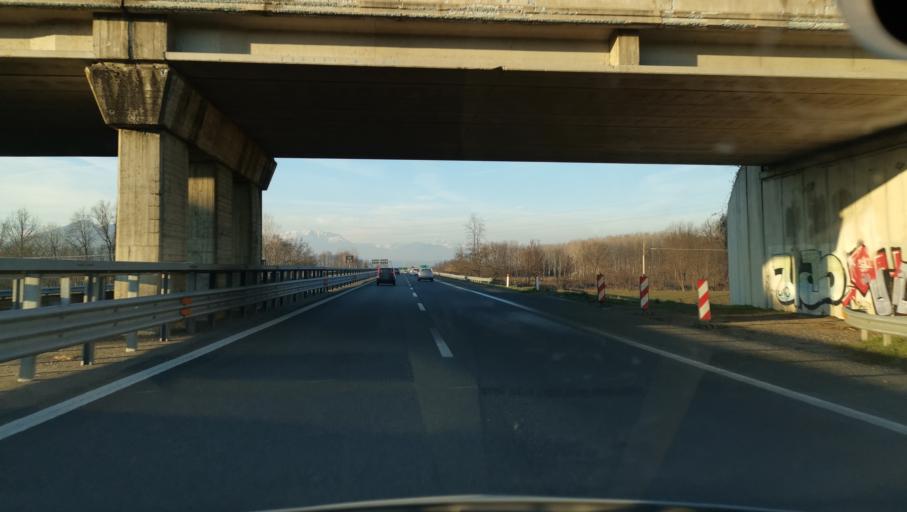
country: IT
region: Piedmont
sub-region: Provincia di Torino
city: Volvera
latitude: 44.9441
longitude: 7.5039
